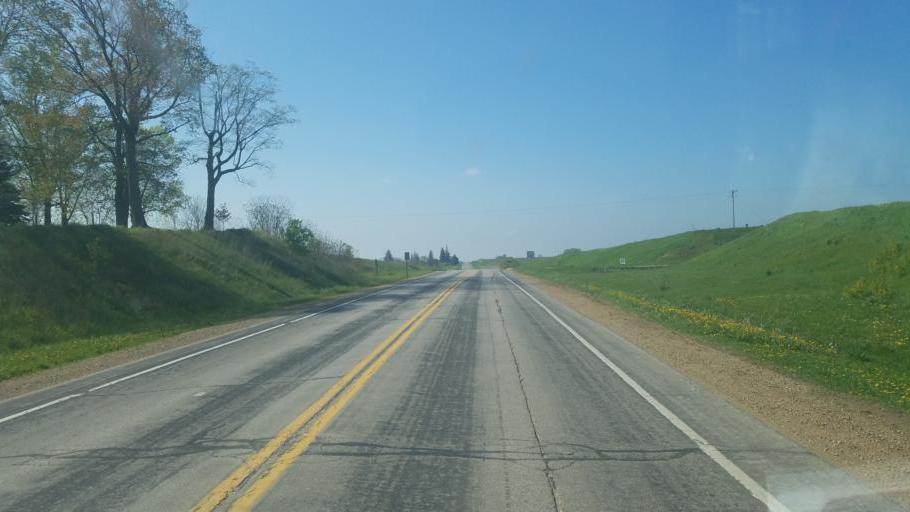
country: US
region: Wisconsin
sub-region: Vernon County
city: Hillsboro
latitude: 43.5873
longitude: -90.3522
